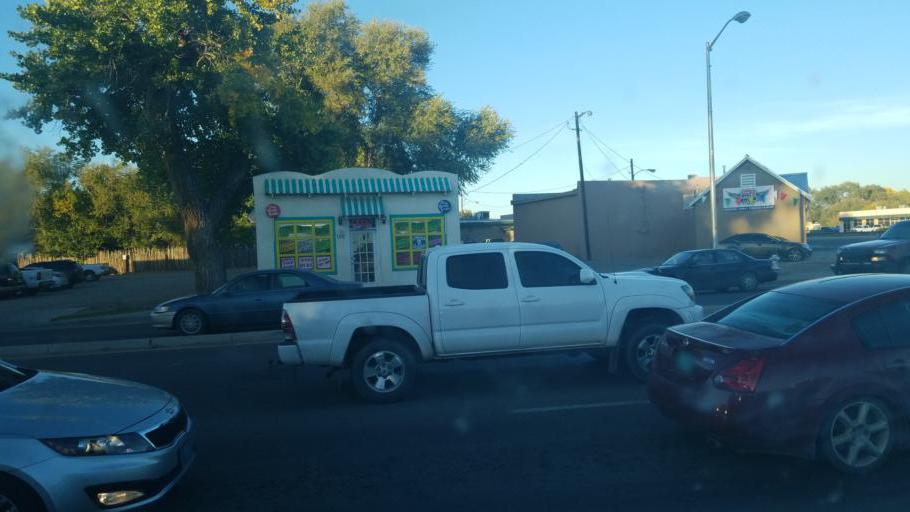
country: US
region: New Mexico
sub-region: Valencia County
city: Los Lunas
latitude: 34.8076
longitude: -106.7364
